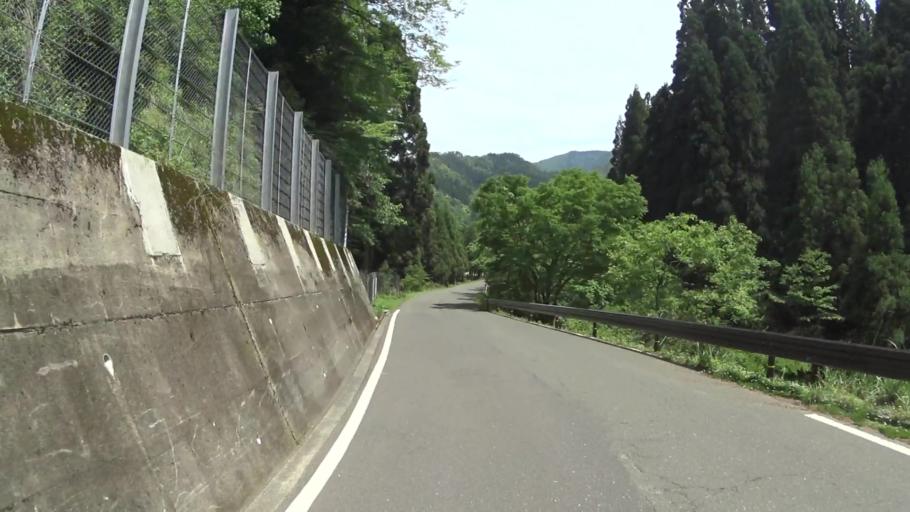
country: JP
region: Kyoto
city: Maizuru
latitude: 35.4407
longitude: 135.5113
